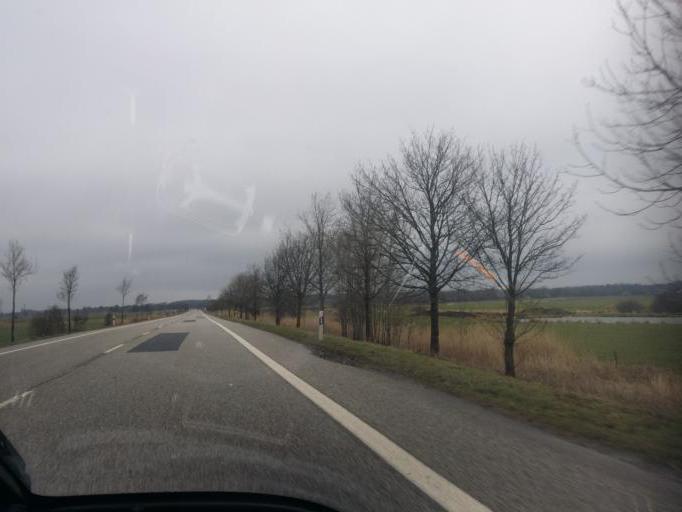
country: DE
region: Schleswig-Holstein
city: Bargum
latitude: 54.7169
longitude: 8.9563
